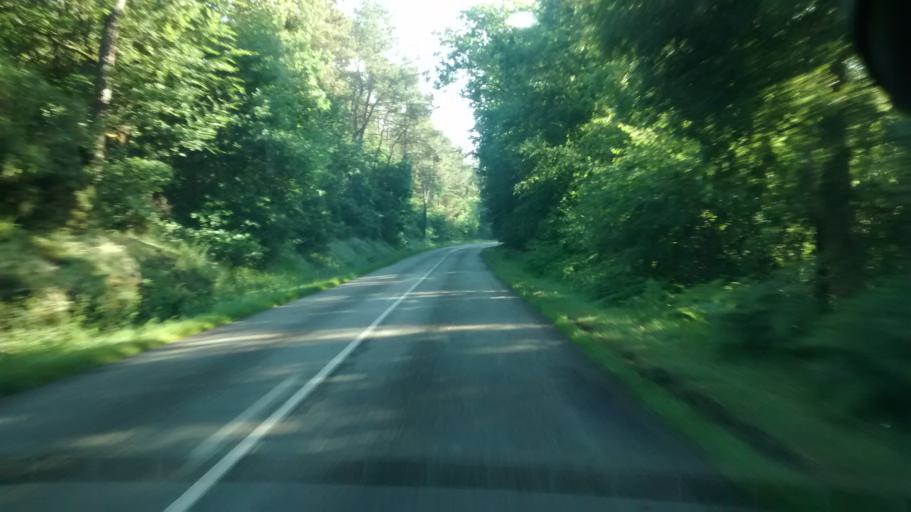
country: FR
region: Brittany
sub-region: Departement du Morbihan
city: Molac
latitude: 47.7718
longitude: -2.4331
